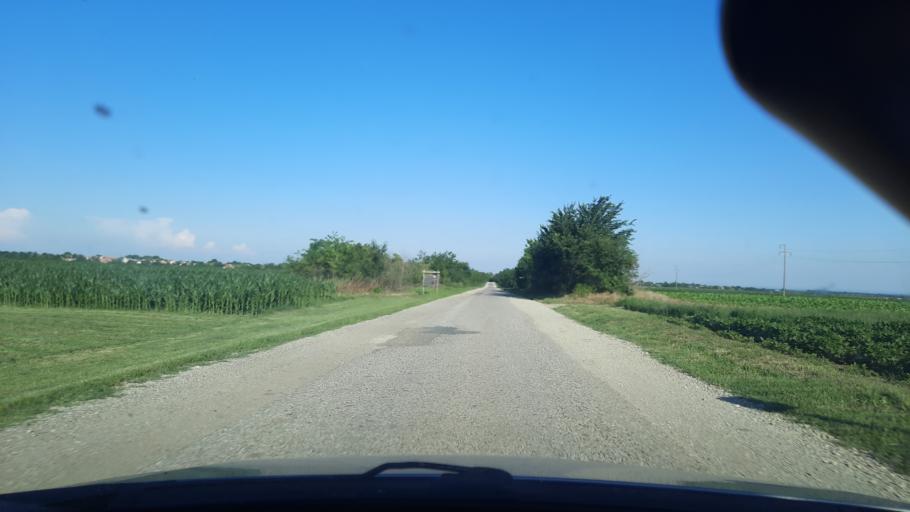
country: RS
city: Cortanovci
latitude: 45.1100
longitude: 19.9739
